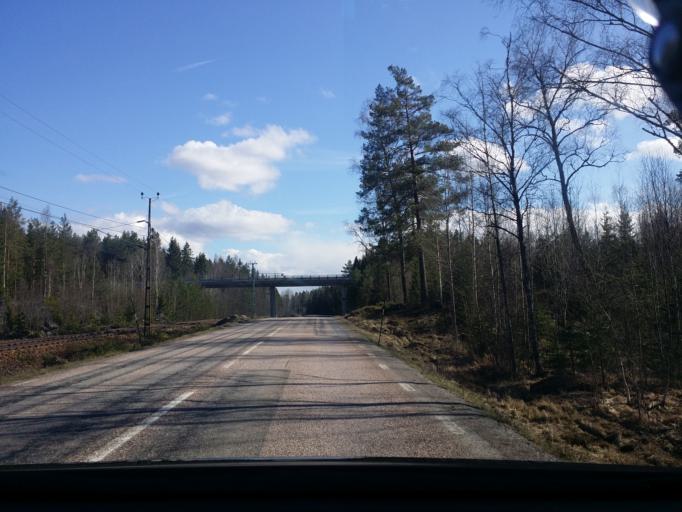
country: SE
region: Vaestmanland
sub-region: Sala Kommun
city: Sala
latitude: 59.9700
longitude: 16.5035
